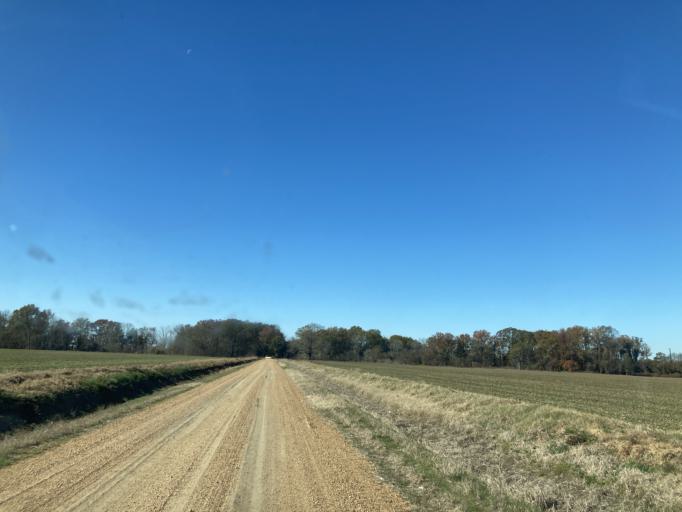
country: US
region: Mississippi
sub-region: Sharkey County
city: Rolling Fork
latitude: 32.8499
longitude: -90.6919
